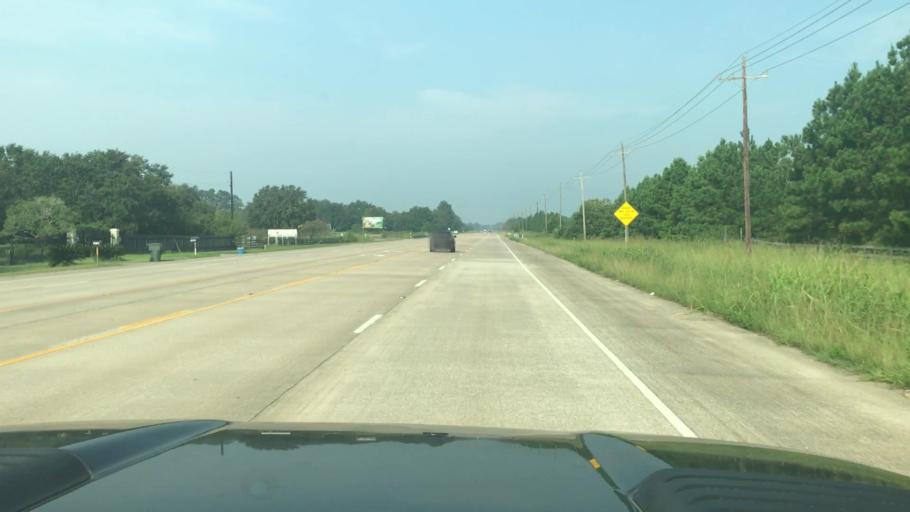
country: US
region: Texas
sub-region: Jefferson County
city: Bevil Oaks
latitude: 30.1331
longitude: -94.2210
